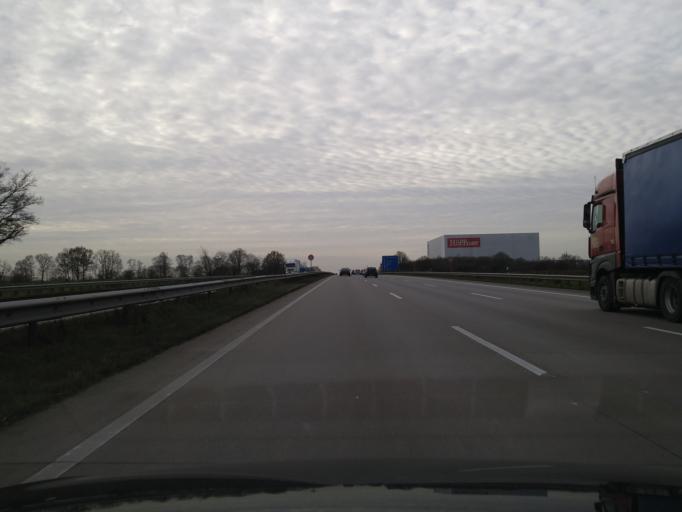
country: DE
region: Schleswig-Holstein
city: Stapelfeld
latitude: 53.5837
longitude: 10.2082
